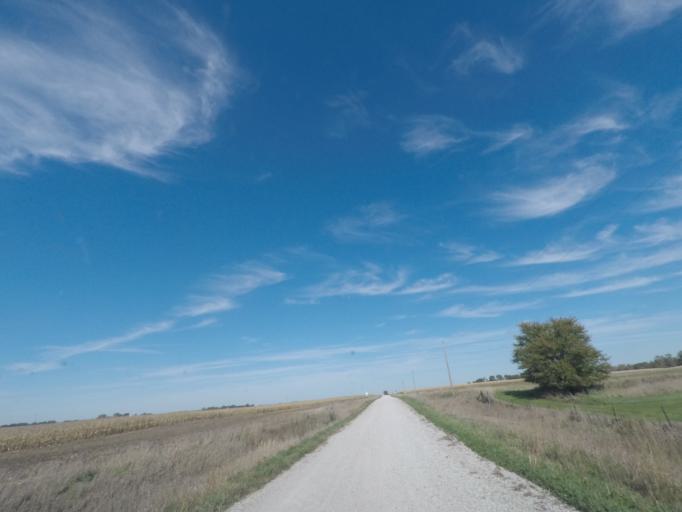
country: US
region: Iowa
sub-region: Story County
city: Nevada
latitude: 42.0129
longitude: -93.3573
